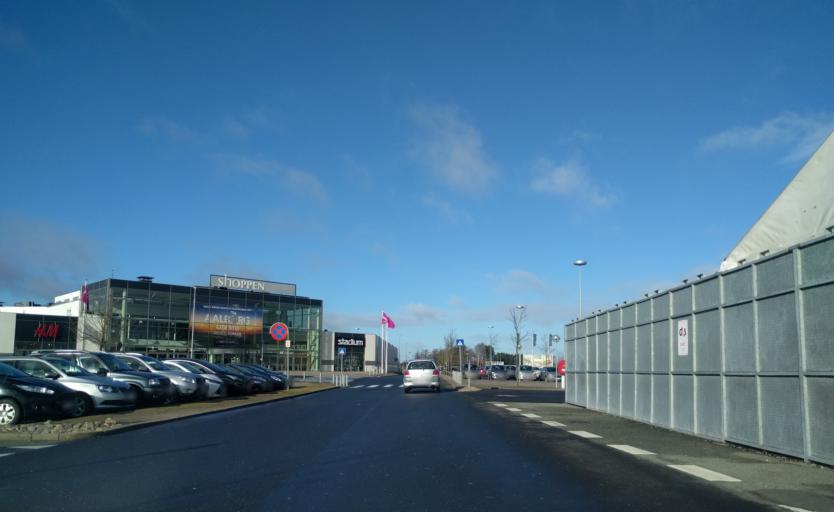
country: DK
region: North Denmark
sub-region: Alborg Kommune
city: Svenstrup
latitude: 57.0033
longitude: 9.8743
